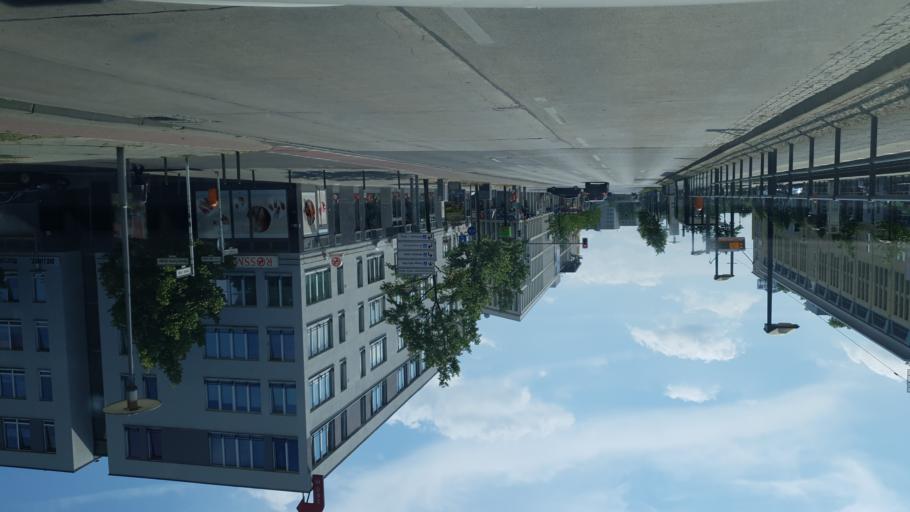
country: DE
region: Berlin
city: Hellersdorf
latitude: 52.5394
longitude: 13.6041
